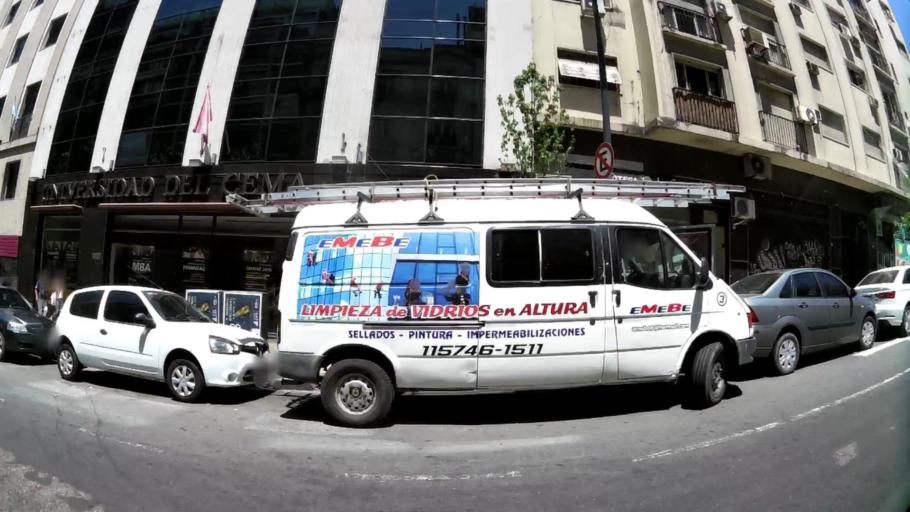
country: AR
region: Buenos Aires F.D.
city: Buenos Aires
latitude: -34.5985
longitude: -58.3725
